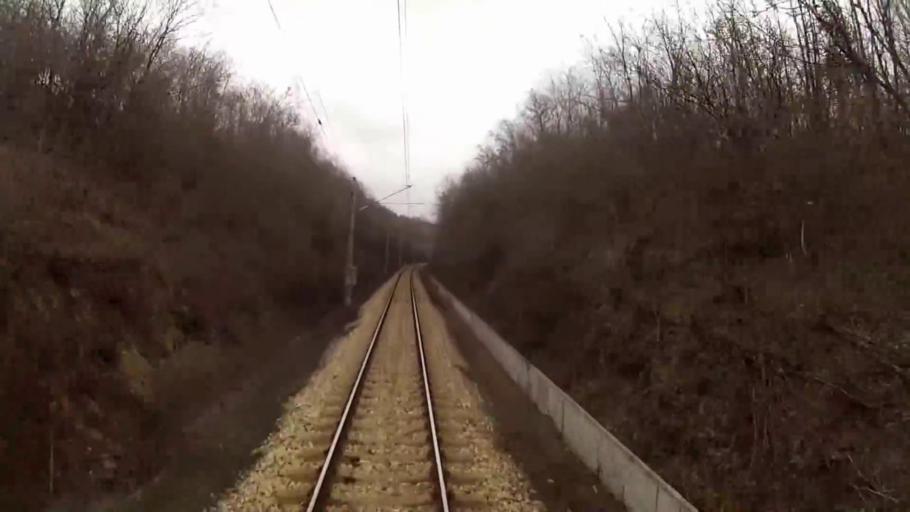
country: BG
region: Sofiya
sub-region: Obshtina Mirkovo
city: Mirkovo
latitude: 42.6996
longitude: 23.9629
